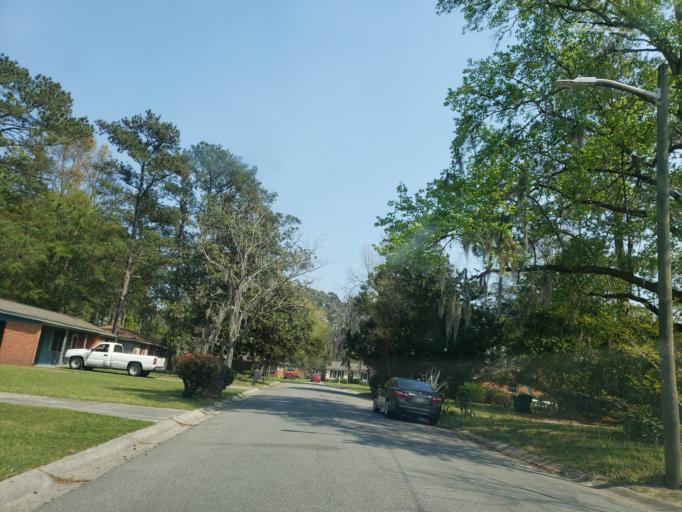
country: US
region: Georgia
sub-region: Chatham County
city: Isle of Hope
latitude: 32.0068
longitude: -81.0724
